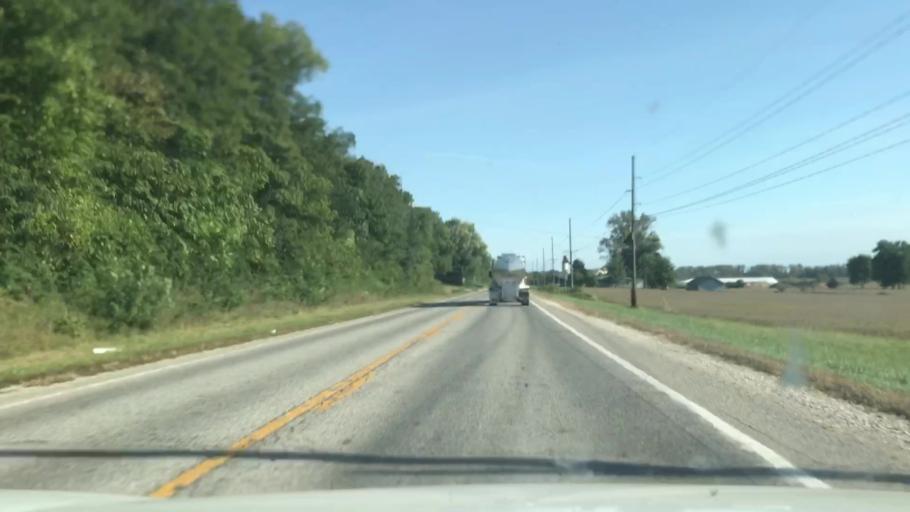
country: US
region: Illinois
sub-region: Adams County
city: Quincy
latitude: 39.8539
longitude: -91.3830
